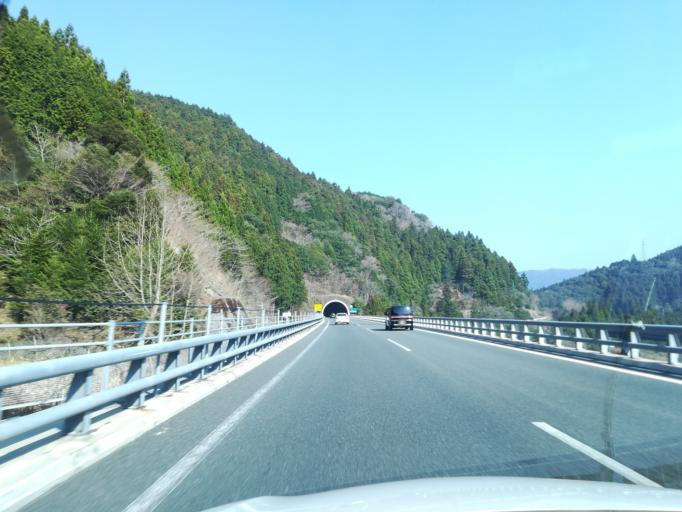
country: JP
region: Ehime
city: Kawanoecho
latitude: 33.8295
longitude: 133.6588
